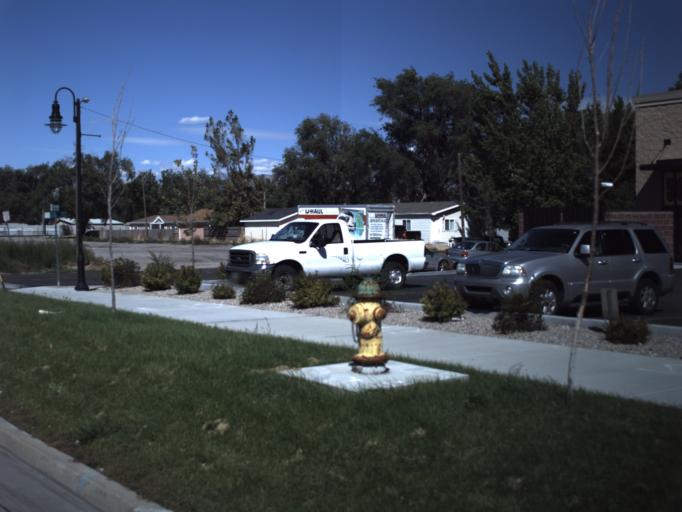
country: US
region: Utah
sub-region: Salt Lake County
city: Taylorsville
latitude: 40.7095
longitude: -111.9388
